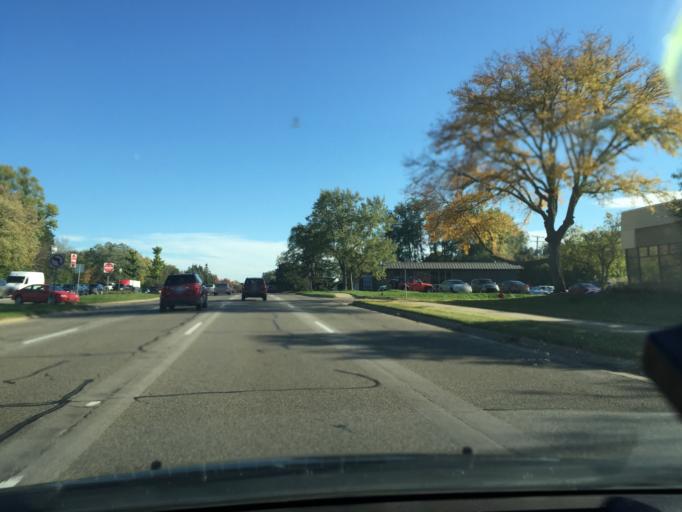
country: US
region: Michigan
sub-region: Oakland County
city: Bloomfield Hills
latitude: 42.6006
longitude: -83.2616
